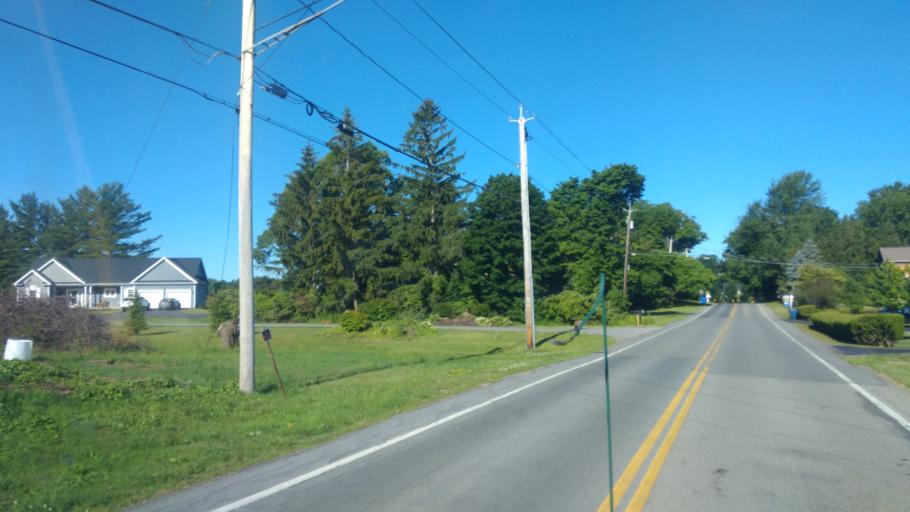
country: US
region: New York
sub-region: Wayne County
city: Williamson
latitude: 43.2802
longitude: -77.1708
